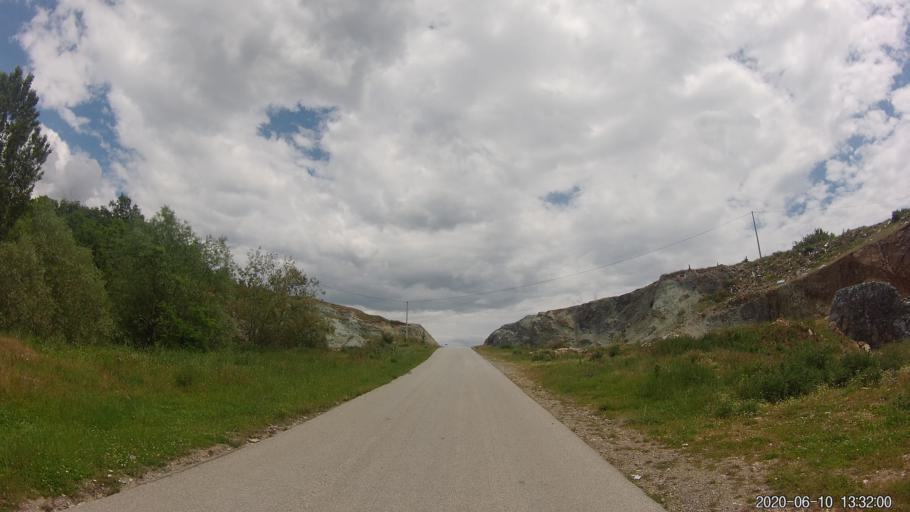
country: XK
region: Prizren
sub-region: Komuna e Therandes
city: Peqan
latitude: 42.4114
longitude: 20.8776
